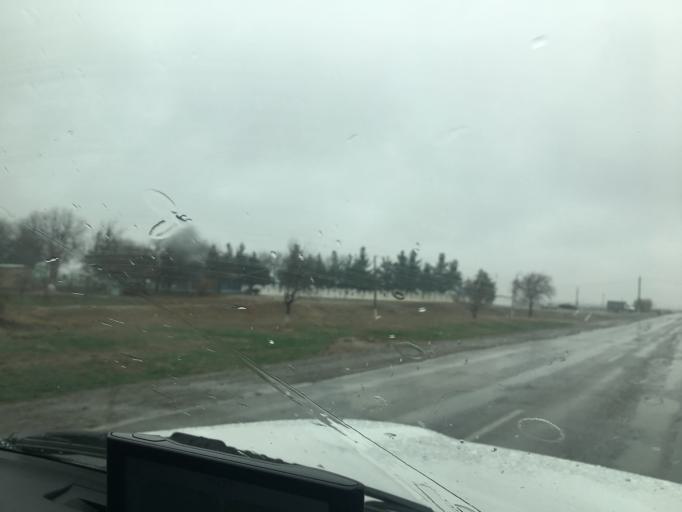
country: TM
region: Mary
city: Yoloeten
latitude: 37.3520
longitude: 62.2522
